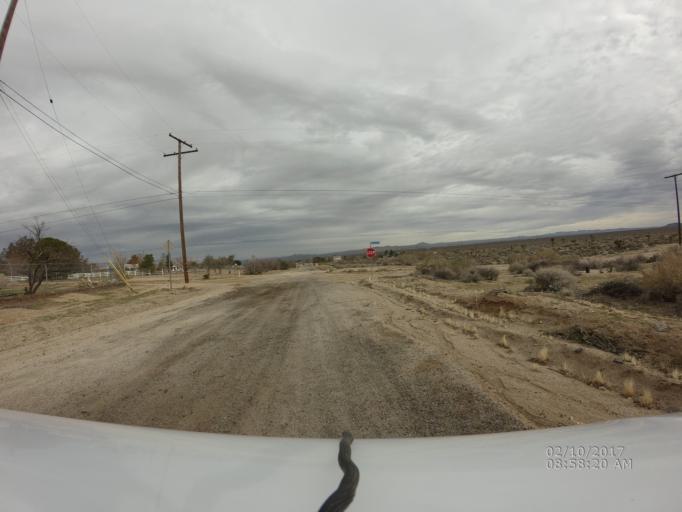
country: US
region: California
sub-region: Los Angeles County
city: Littlerock
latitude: 34.4915
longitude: -117.8900
